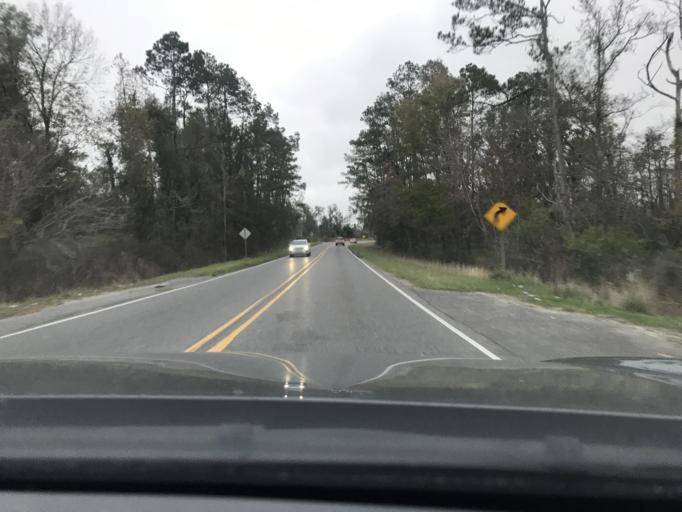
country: US
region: Louisiana
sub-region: Calcasieu Parish
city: Westlake
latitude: 30.2978
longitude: -93.2483
